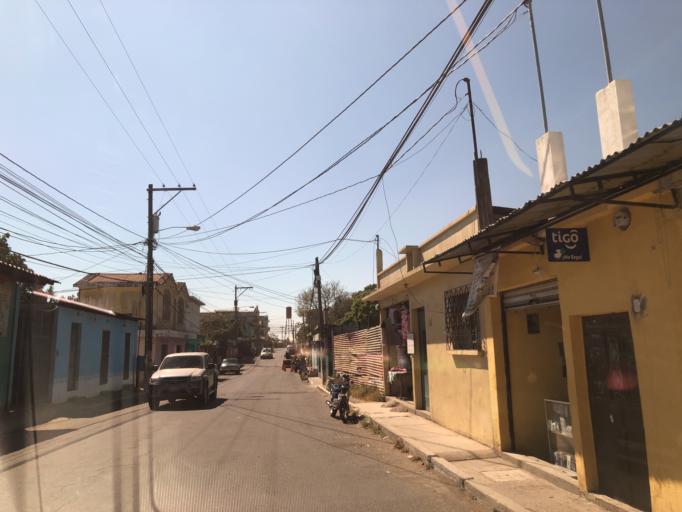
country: GT
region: Guatemala
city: Mixco
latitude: 14.6108
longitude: -90.5757
